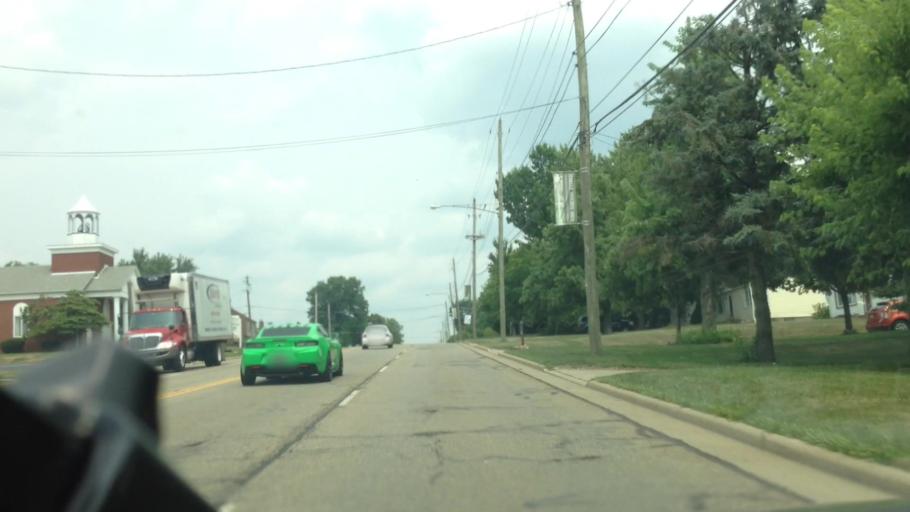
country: US
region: Ohio
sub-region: Stark County
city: Genoa
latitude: 40.7988
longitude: -81.4262
